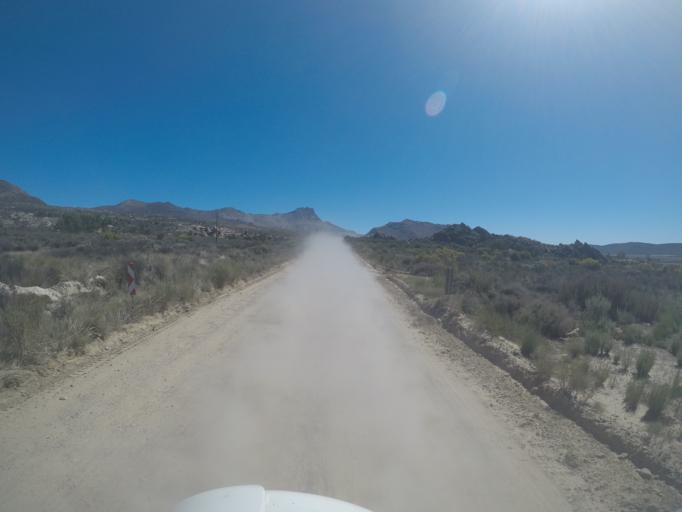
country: ZA
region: Western Cape
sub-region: Cape Winelands District Municipality
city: Ceres
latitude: -32.8780
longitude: 19.4479
